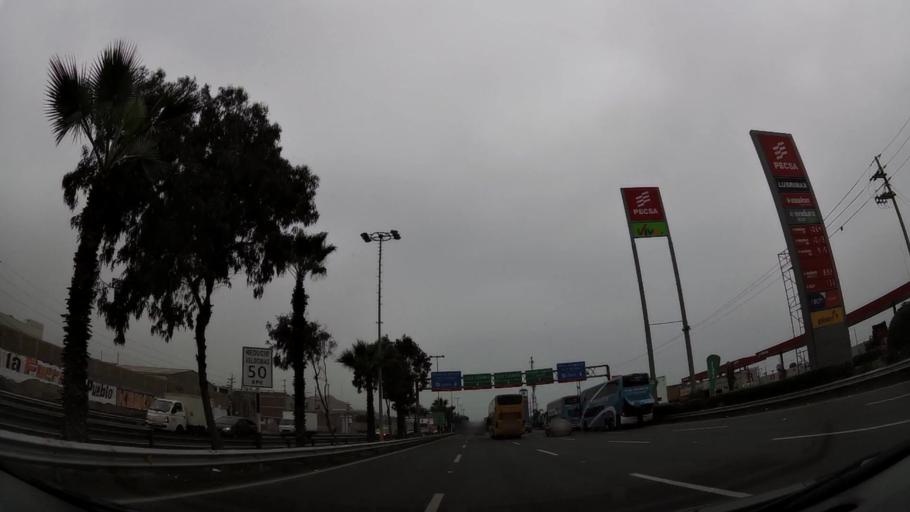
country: PE
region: Lima
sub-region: Lima
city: Surco
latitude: -12.2228
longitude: -76.9745
